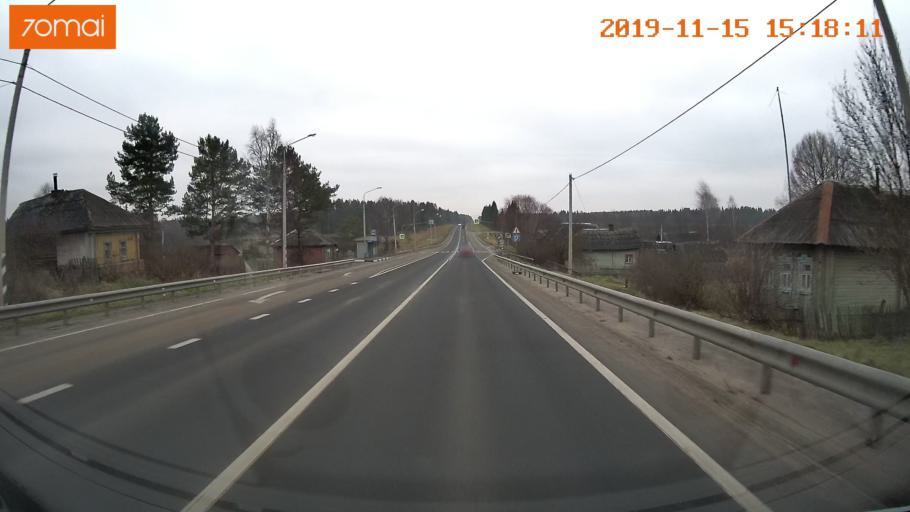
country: RU
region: Jaroslavl
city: Danilov
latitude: 58.2508
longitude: 40.1807
